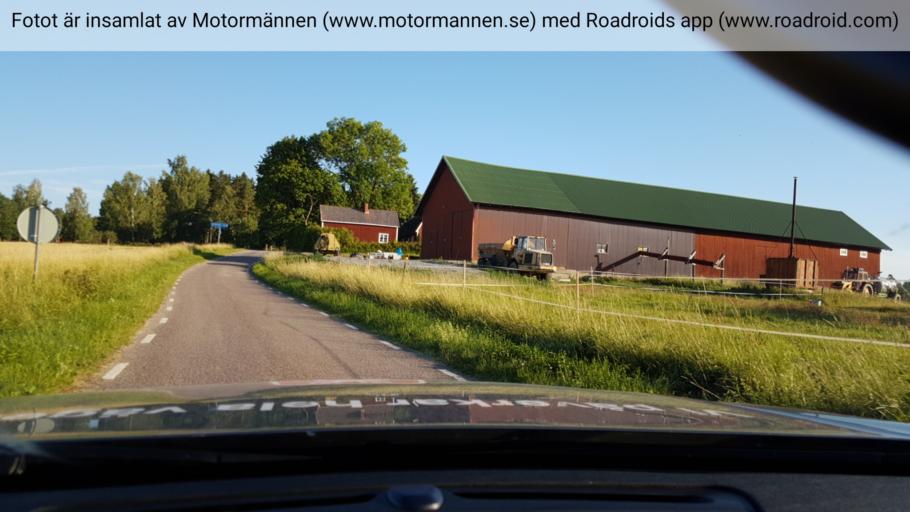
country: SE
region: Vaestmanland
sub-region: Kopings Kommun
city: Koping
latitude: 59.6338
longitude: 16.0611
